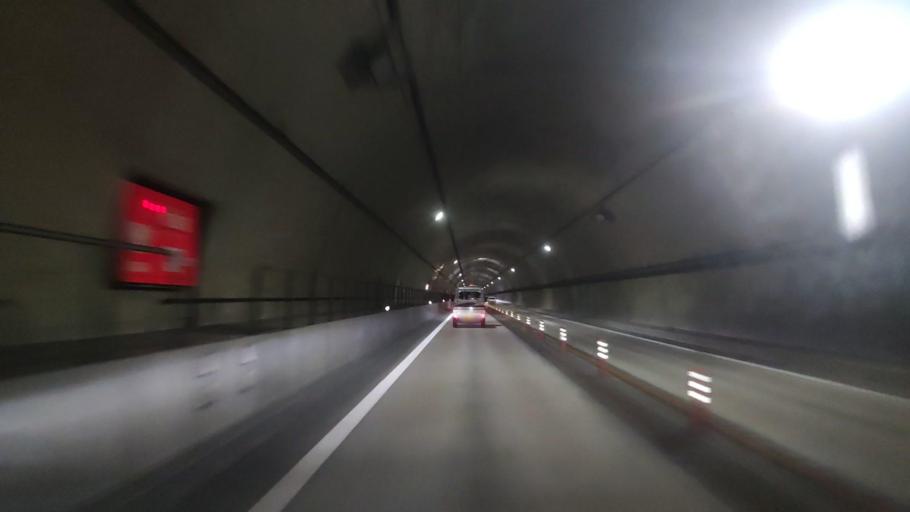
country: JP
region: Wakayama
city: Tanabe
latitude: 33.6169
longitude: 135.4223
